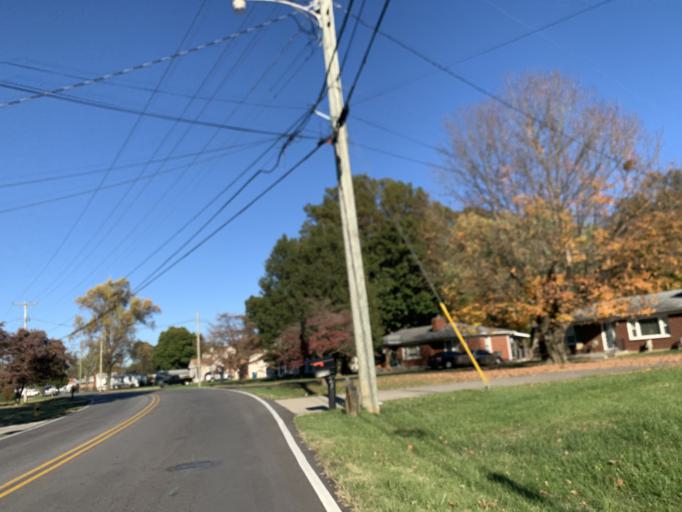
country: US
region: Kentucky
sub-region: Jefferson County
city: Pleasure Ridge Park
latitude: 38.1593
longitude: -85.8461
